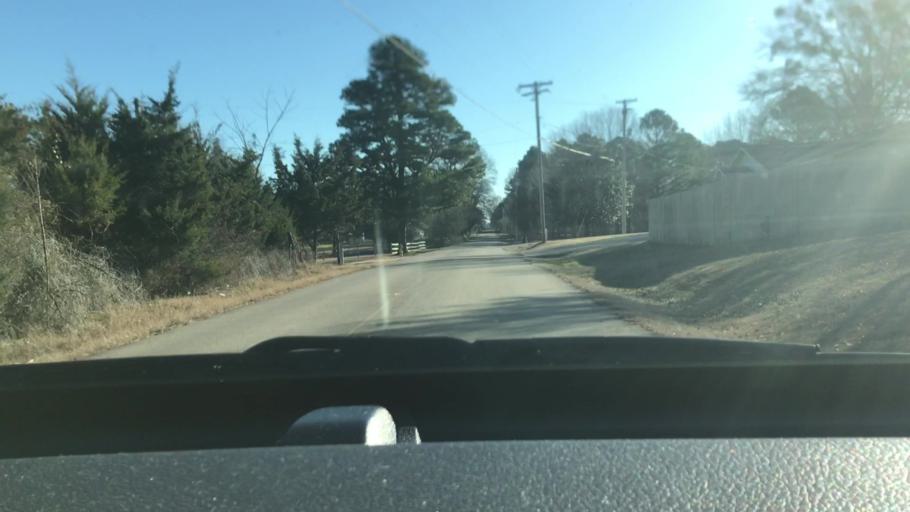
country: US
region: Arkansas
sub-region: Hempstead County
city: Hope
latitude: 33.6389
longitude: -93.5769
